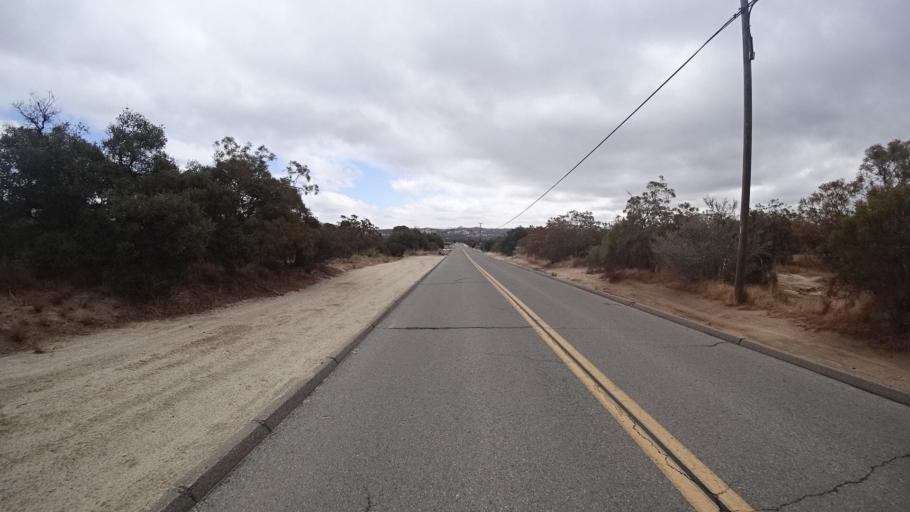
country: US
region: California
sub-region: San Diego County
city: Campo
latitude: 32.6095
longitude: -116.3272
